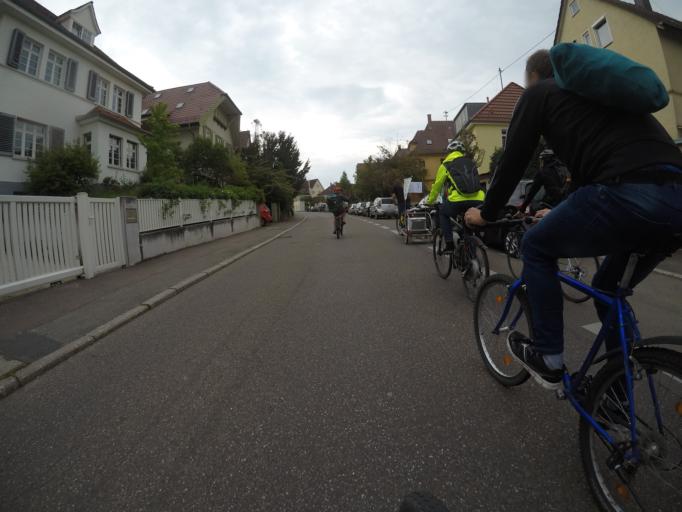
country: DE
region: Baden-Wuerttemberg
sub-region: Regierungsbezirk Stuttgart
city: Esslingen
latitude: 48.7345
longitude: 9.3282
